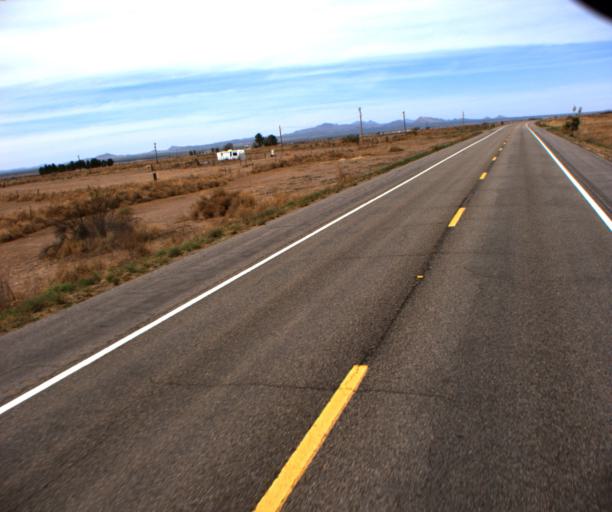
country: US
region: Arizona
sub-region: Cochise County
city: Pirtleville
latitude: 31.5533
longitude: -109.6636
